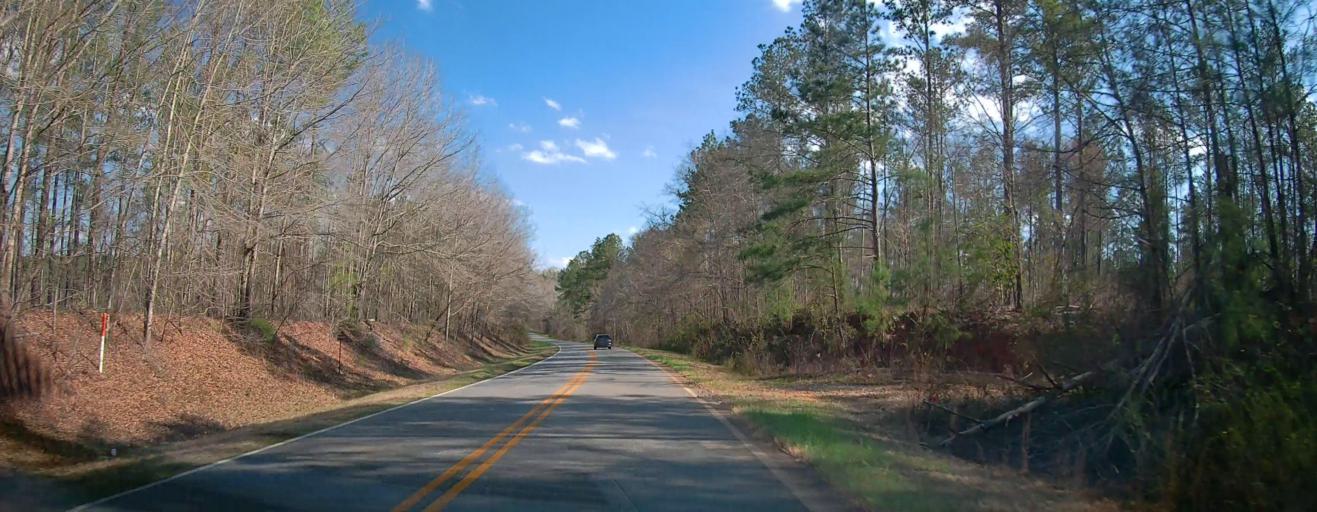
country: US
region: Georgia
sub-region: Laurens County
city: Dublin
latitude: 32.5757
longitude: -83.0479
